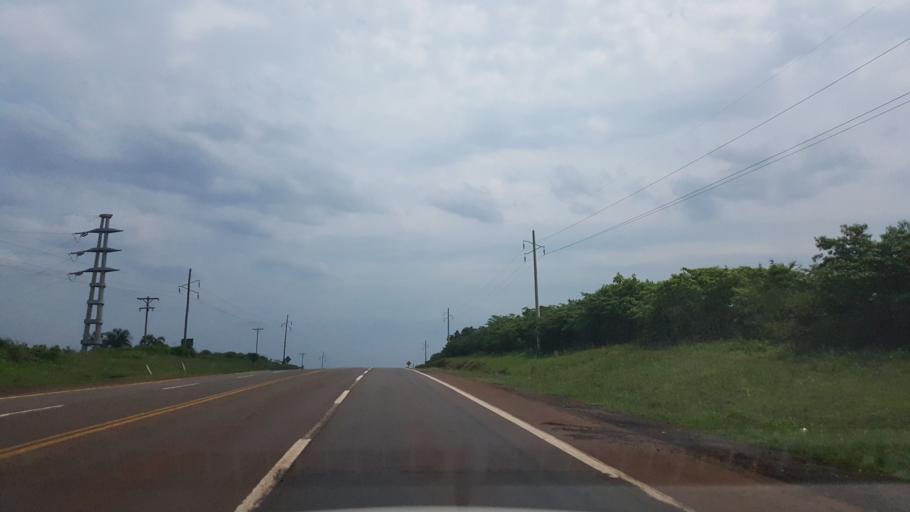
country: AR
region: Misiones
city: Capiovi
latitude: -26.9424
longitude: -55.0821
